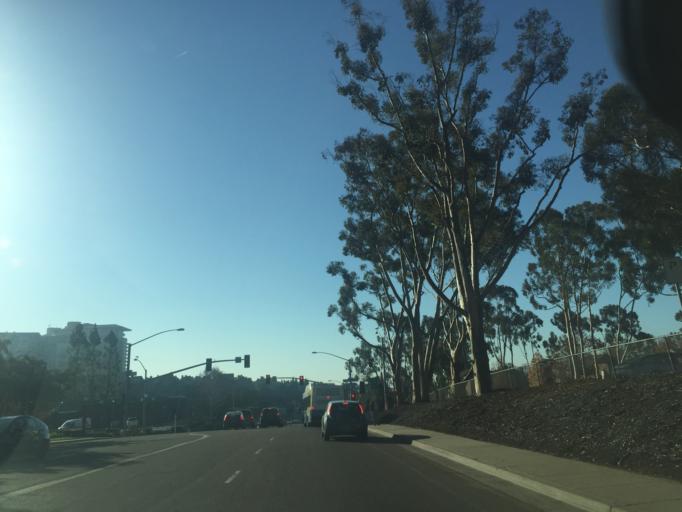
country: US
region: California
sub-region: San Diego County
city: La Jolla
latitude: 32.8734
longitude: -117.2184
